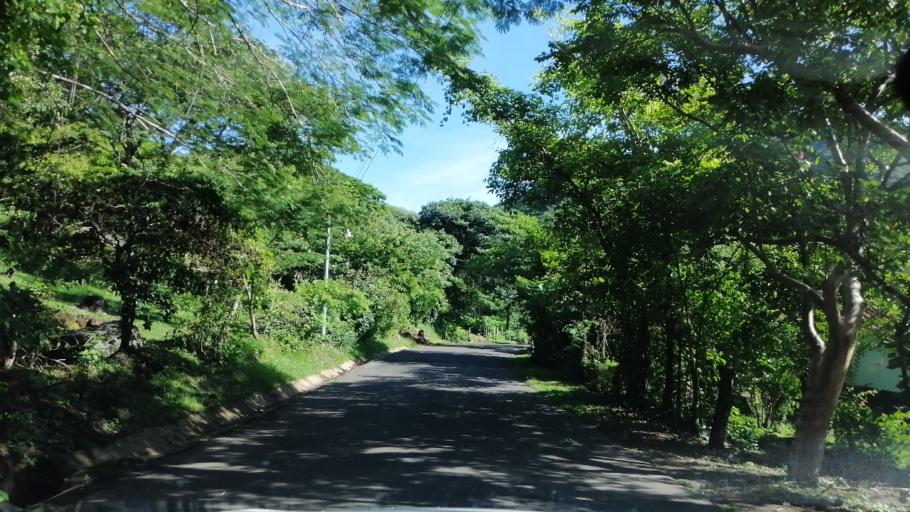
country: SV
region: Morazan
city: Corinto
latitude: 13.7925
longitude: -88.0122
